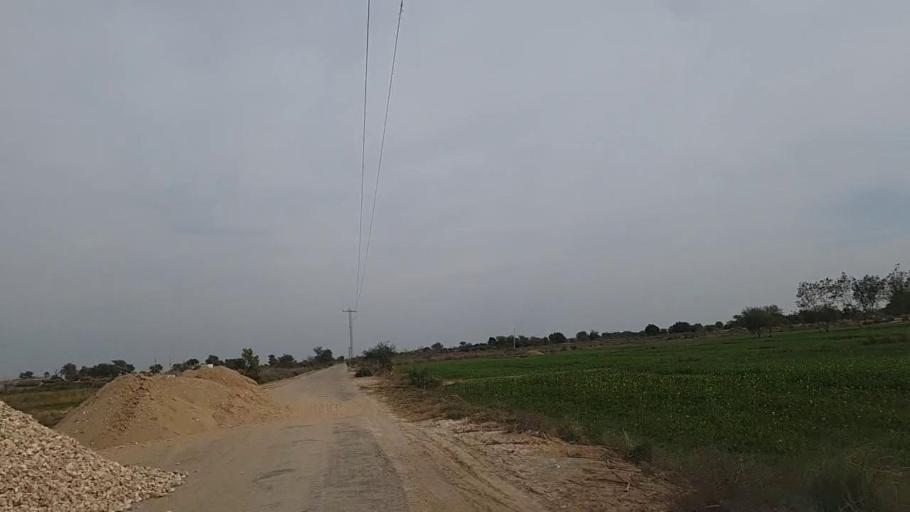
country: PK
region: Sindh
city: Jam Sahib
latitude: 26.4001
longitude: 68.5273
